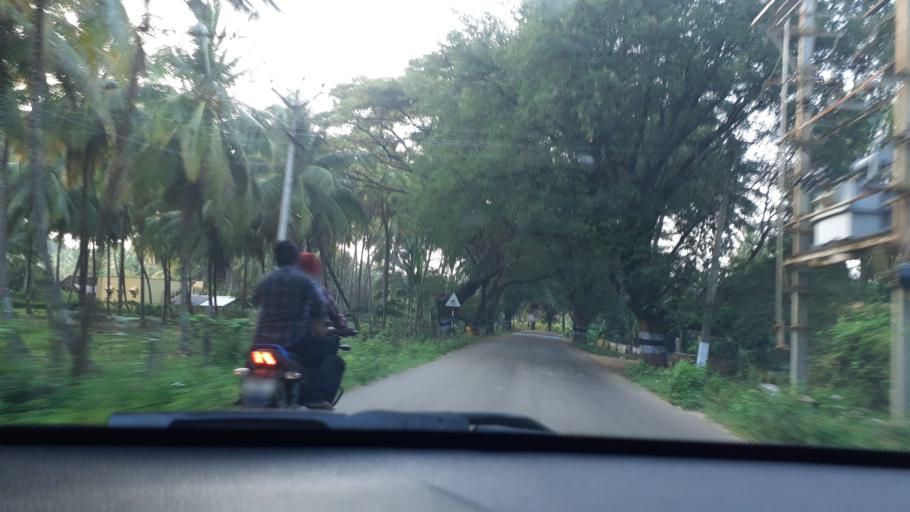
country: IN
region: Tamil Nadu
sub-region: Dindigul
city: Ayakudi
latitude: 10.4148
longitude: 77.5378
